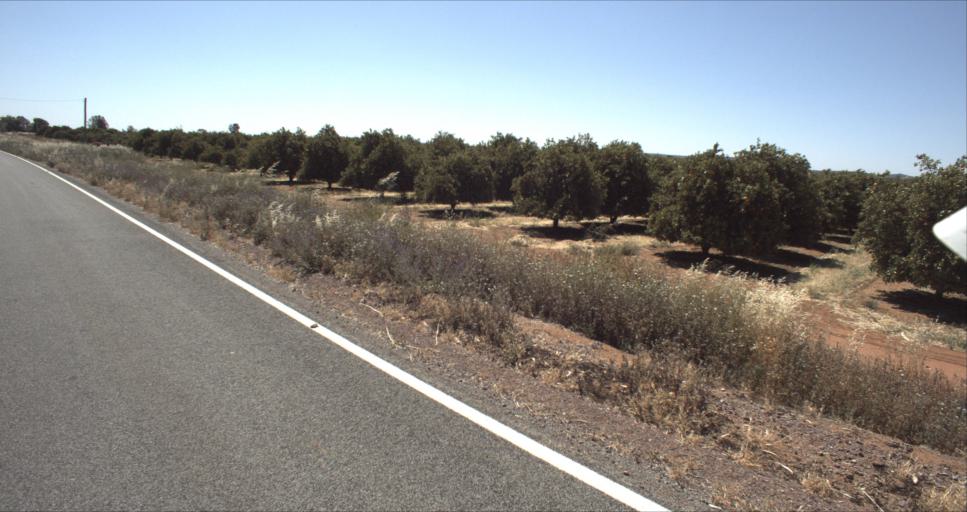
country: AU
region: New South Wales
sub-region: Leeton
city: Leeton
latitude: -34.5186
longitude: 146.4364
